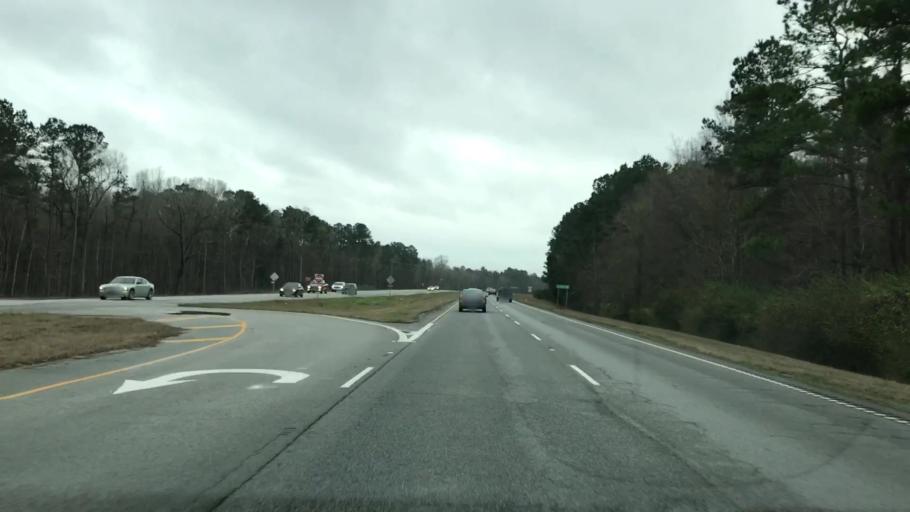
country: US
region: South Carolina
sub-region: Berkeley County
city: Moncks Corner
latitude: 33.1238
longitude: -80.0291
